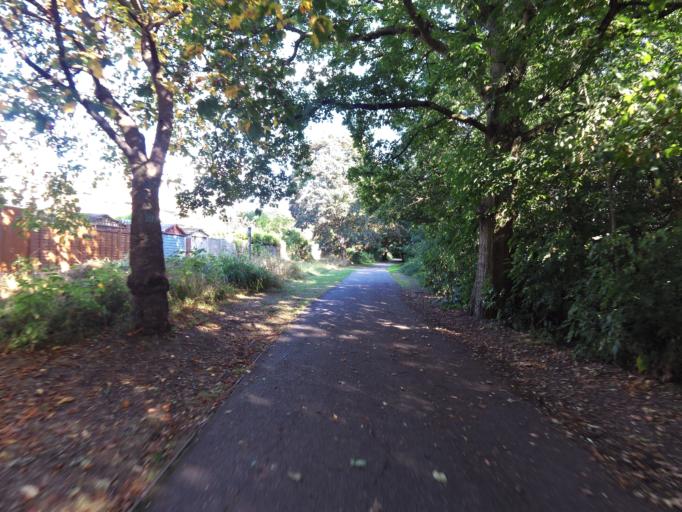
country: GB
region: England
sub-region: Greater London
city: Wood Green
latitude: 51.6246
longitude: -0.1394
